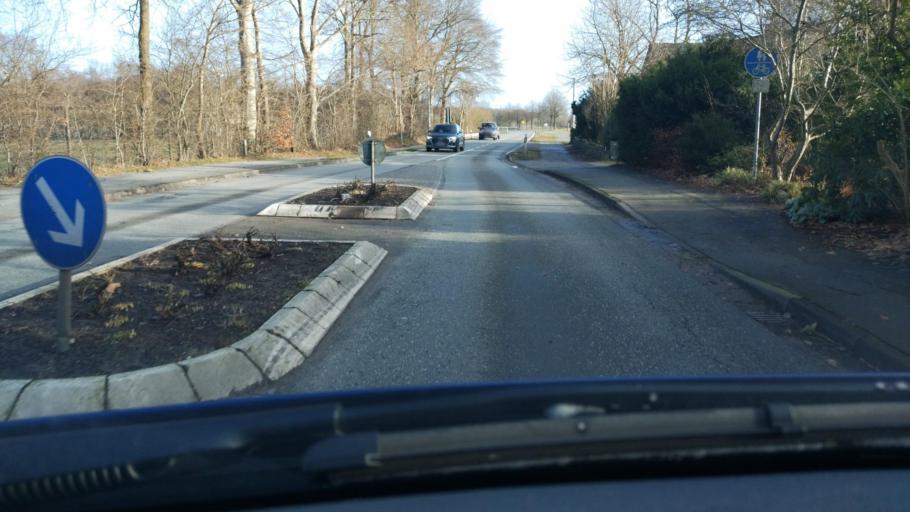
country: DE
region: Schleswig-Holstein
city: Wanderup
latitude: 54.6882
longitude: 9.3395
